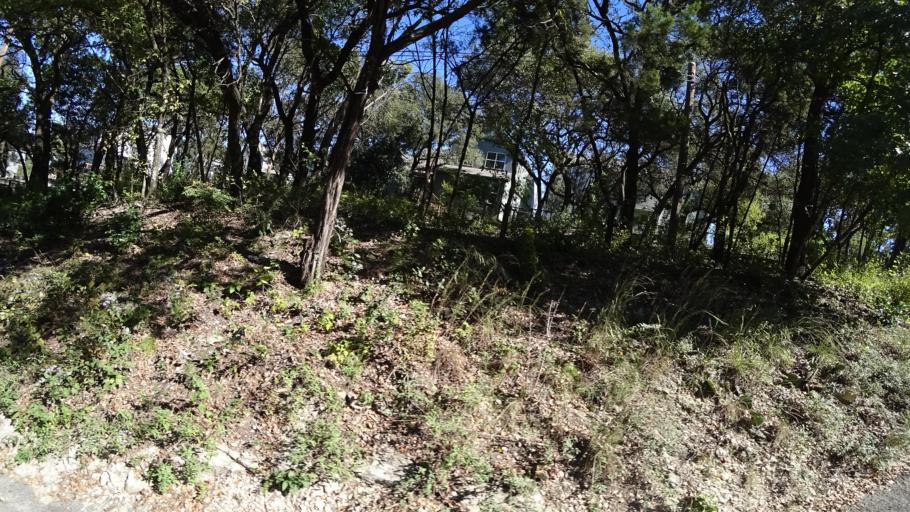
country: US
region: Texas
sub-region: Travis County
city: Rollingwood
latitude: 30.2405
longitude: -97.7791
